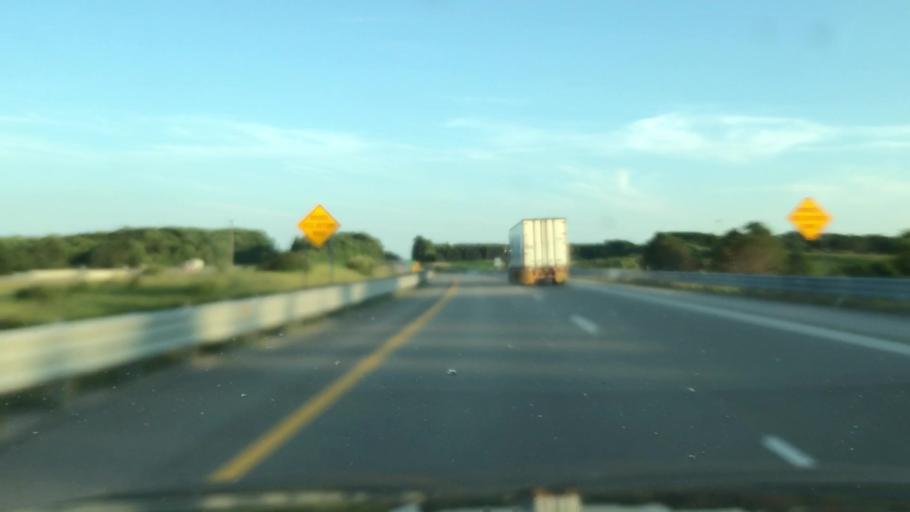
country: US
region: Michigan
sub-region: Osceola County
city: Reed City
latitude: 43.8609
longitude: -85.5355
